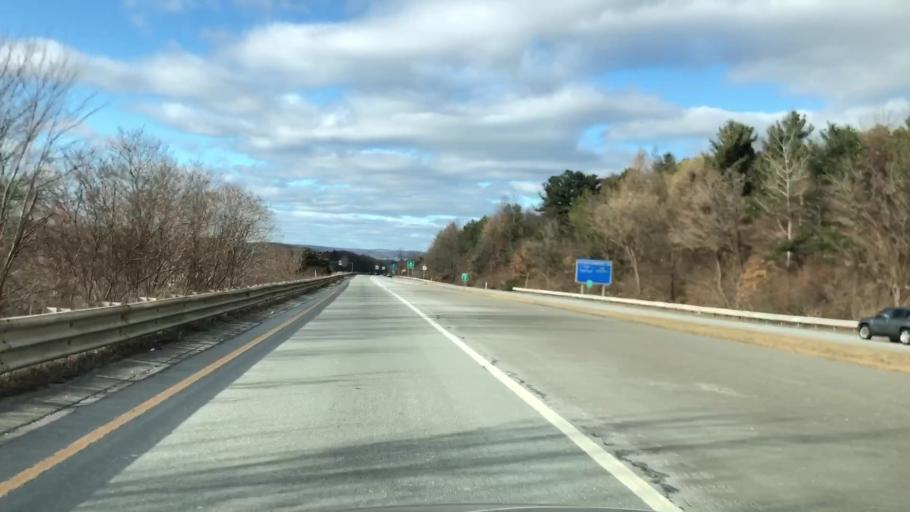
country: US
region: Massachusetts
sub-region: Worcester County
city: Leominster
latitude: 42.5258
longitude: -71.7295
